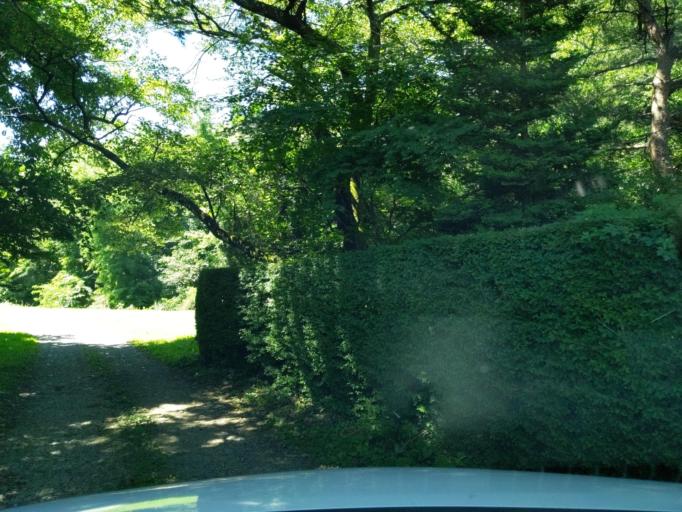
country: JP
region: Fukushima
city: Koriyama
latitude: 37.3912
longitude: 140.2611
